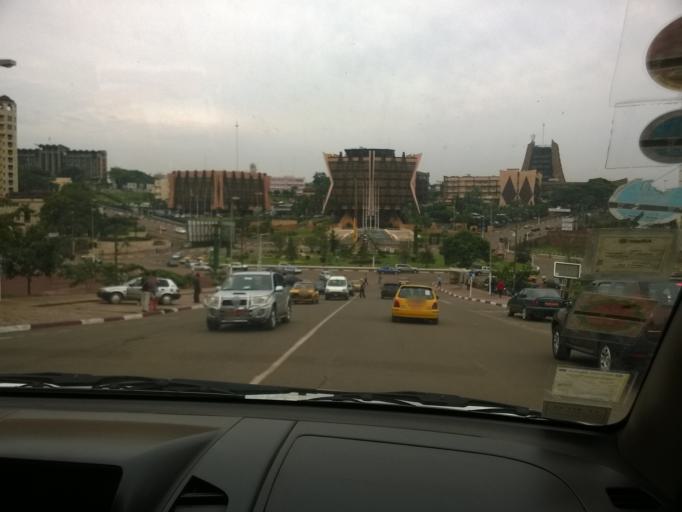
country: CM
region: Centre
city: Yaounde
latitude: 3.8665
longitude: 11.5154
